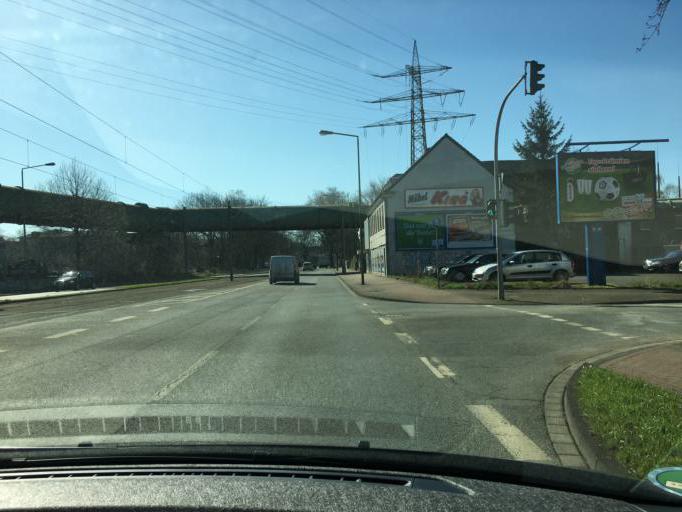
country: DE
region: North Rhine-Westphalia
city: Meiderich
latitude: 51.4613
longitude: 6.7331
